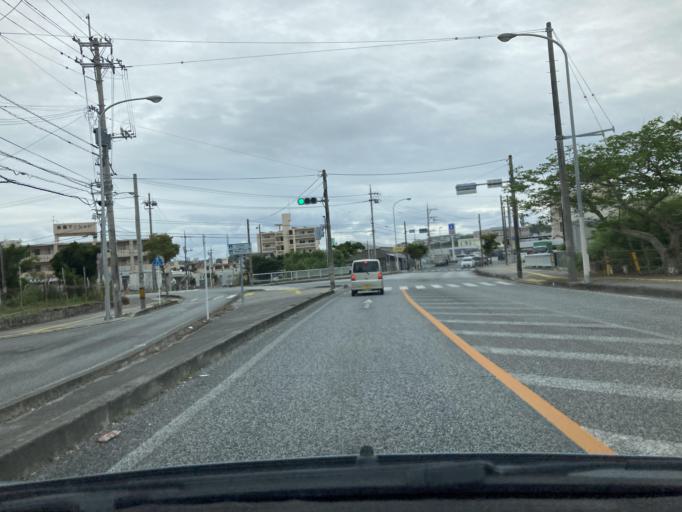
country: JP
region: Okinawa
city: Tomigusuku
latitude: 26.1794
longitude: 127.7176
